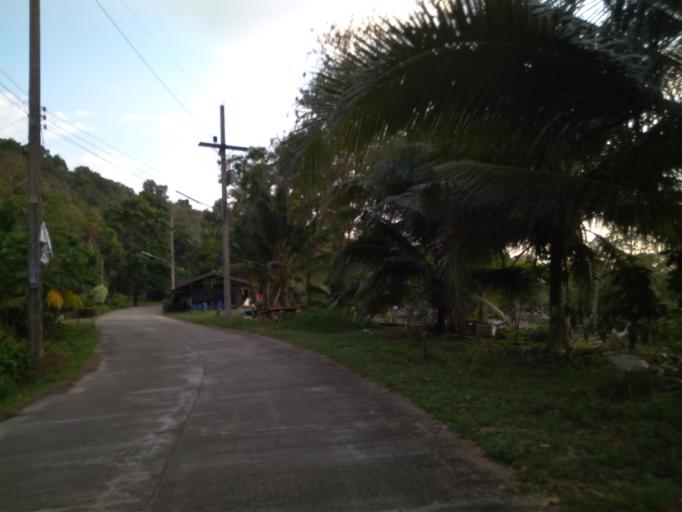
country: TH
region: Phangnga
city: Ko Yao
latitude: 8.1487
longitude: 98.5988
